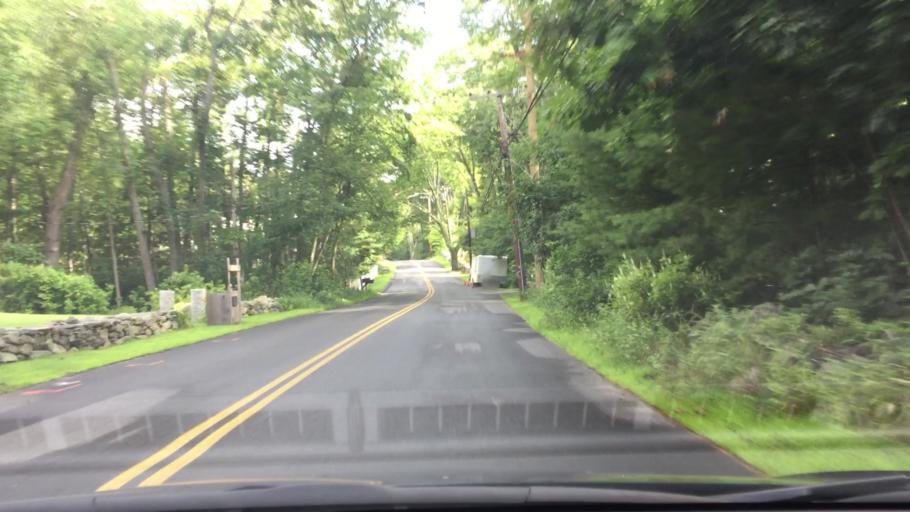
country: US
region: Massachusetts
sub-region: Middlesex County
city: Acton
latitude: 42.4949
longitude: -71.4366
